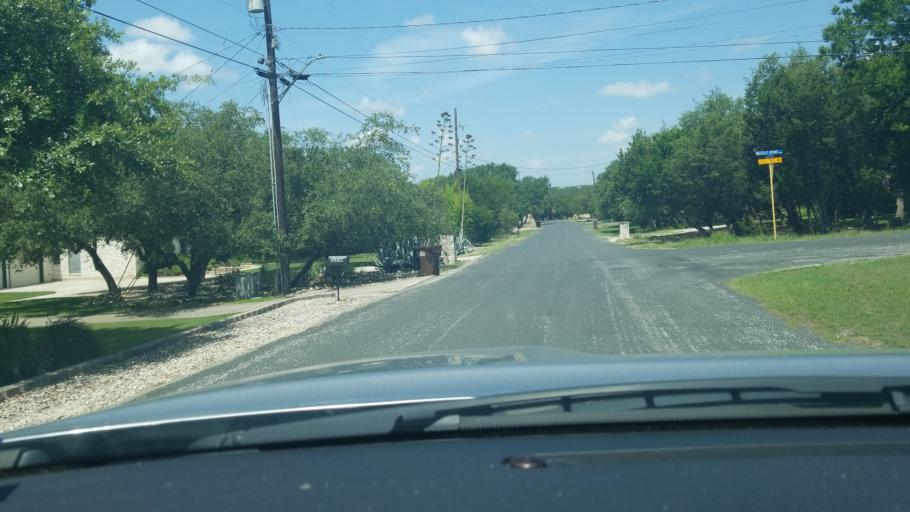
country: US
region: Texas
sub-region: Bexar County
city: Timberwood Park
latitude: 29.6894
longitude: -98.4870
